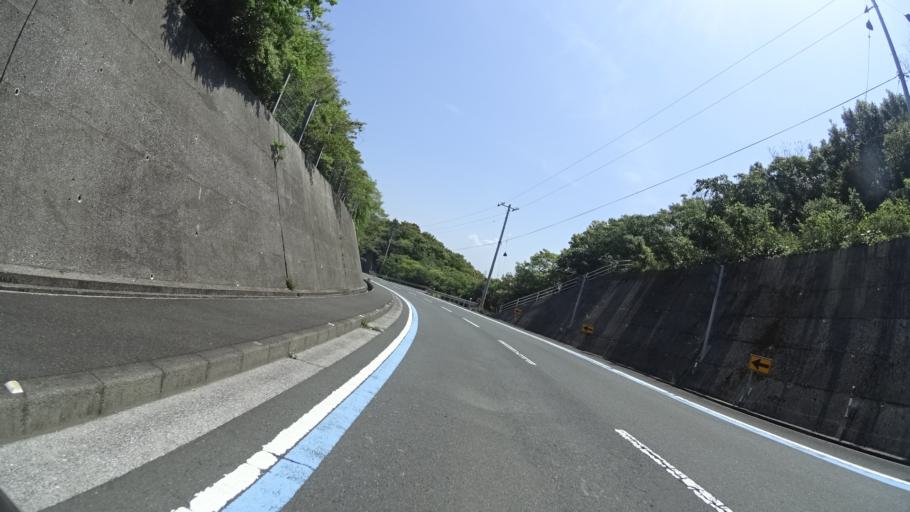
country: JP
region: Ehime
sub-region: Nishiuwa-gun
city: Ikata-cho
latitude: 33.4404
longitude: 132.2434
